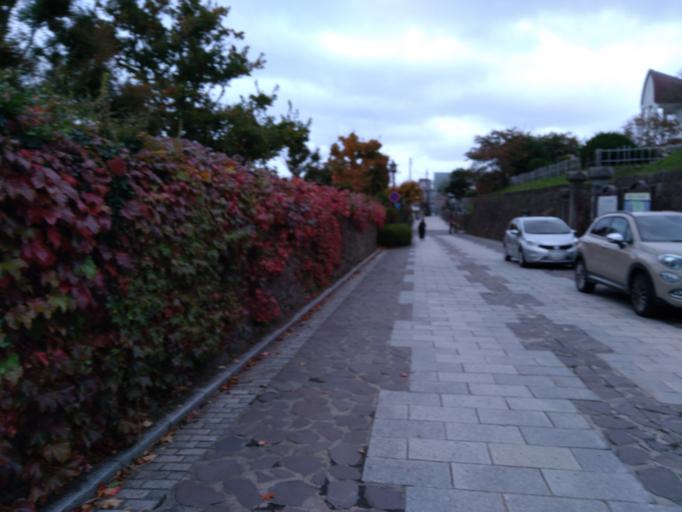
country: JP
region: Hokkaido
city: Hakodate
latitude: 41.7633
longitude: 140.7124
